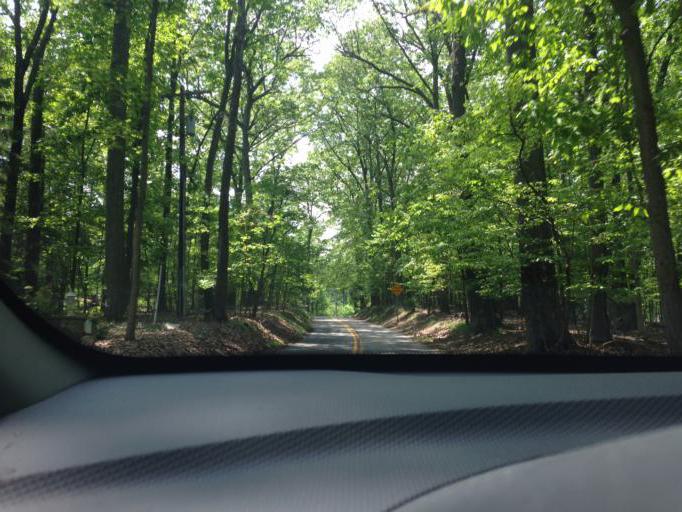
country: US
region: Maryland
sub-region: Baltimore County
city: Cockeysville
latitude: 39.4763
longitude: -76.6852
